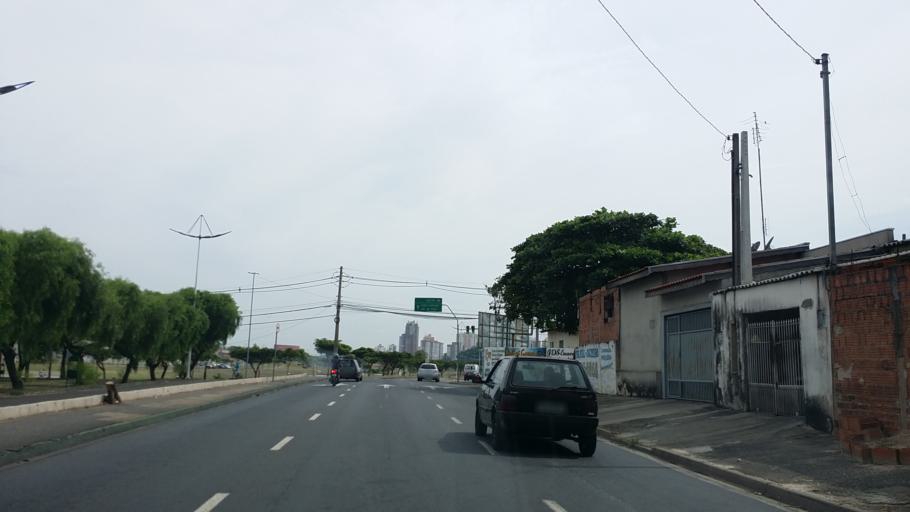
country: BR
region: Sao Paulo
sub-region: Indaiatuba
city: Indaiatuba
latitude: -23.1109
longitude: -47.2302
